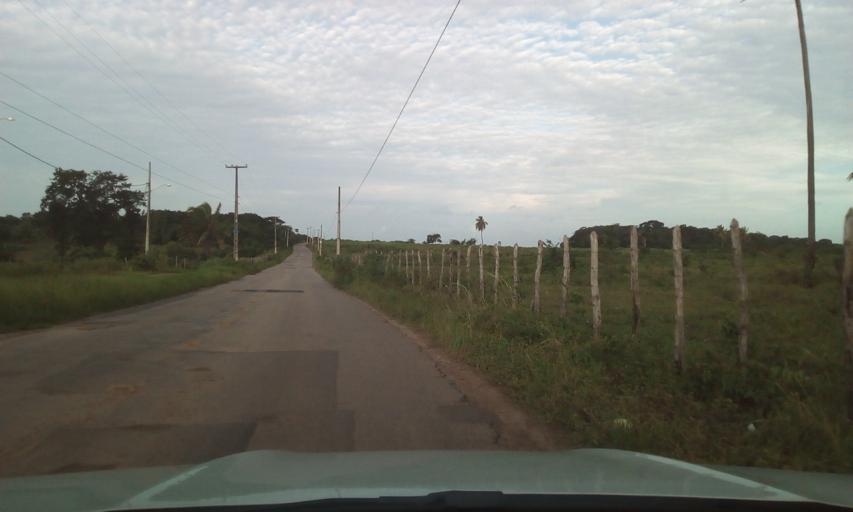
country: BR
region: Paraiba
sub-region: Conde
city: Conde
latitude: -7.2208
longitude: -34.8319
